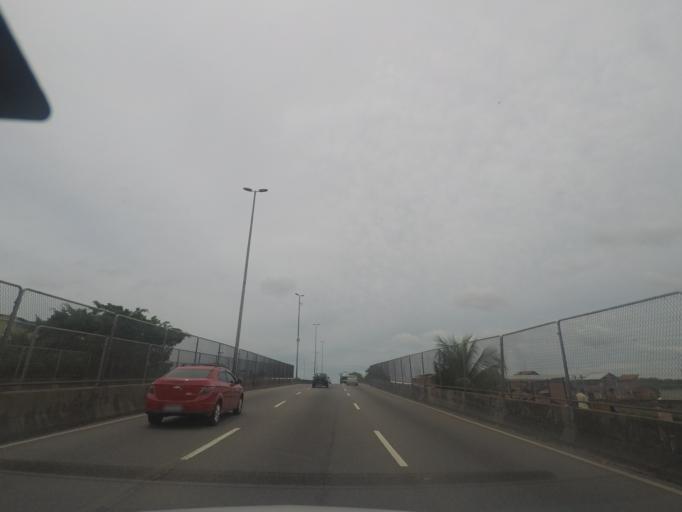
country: BR
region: Rio de Janeiro
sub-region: Sao Joao De Meriti
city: Sao Joao de Meriti
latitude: -22.9527
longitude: -43.3571
